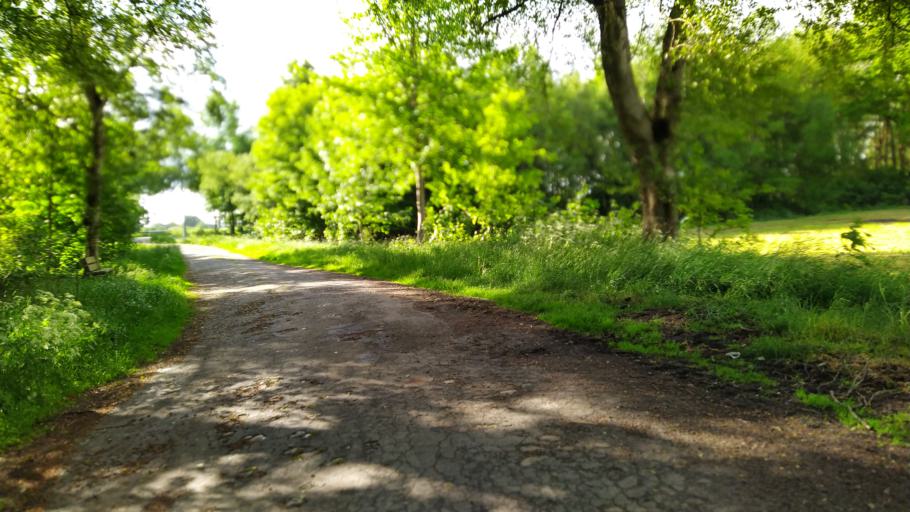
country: DE
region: Lower Saxony
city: Brest
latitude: 53.4385
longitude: 9.3524
